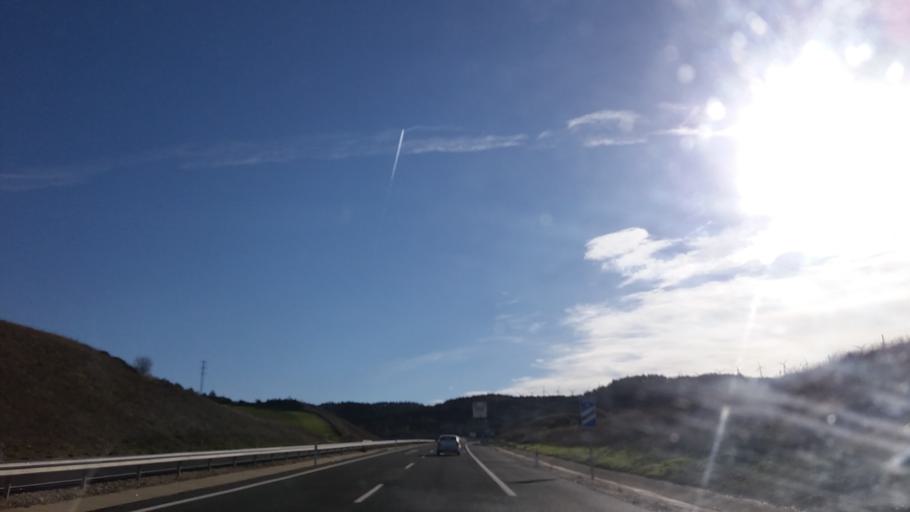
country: ES
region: Navarre
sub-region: Provincia de Navarra
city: Leache
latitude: 42.6602
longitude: -1.4215
